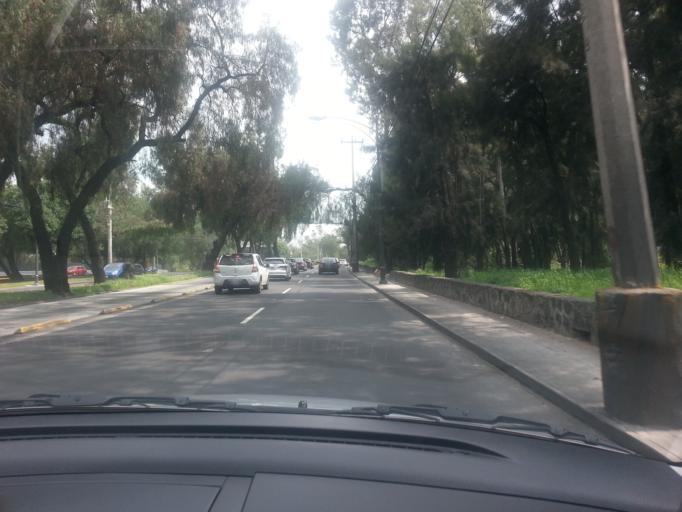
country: MX
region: Mexico City
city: Magdalena Contreras
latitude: 19.3296
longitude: -99.1894
